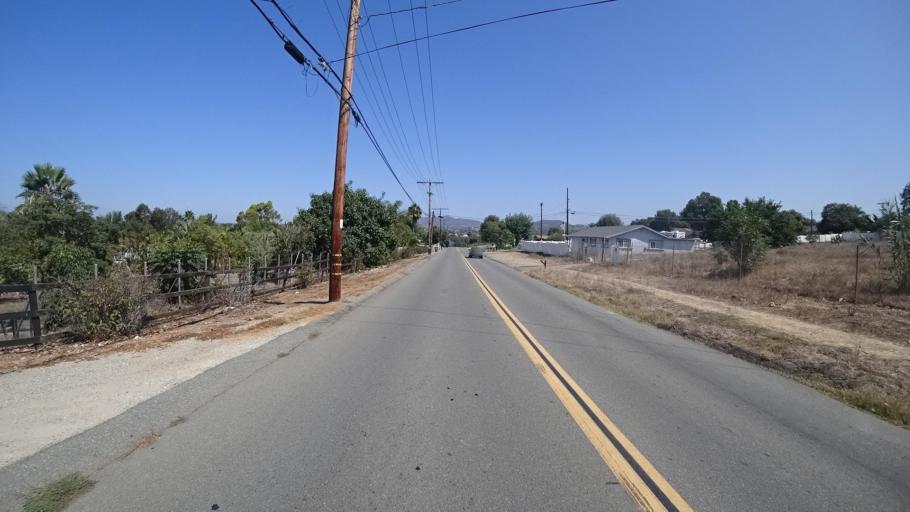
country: US
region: California
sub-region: San Diego County
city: Lake San Marcos
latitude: 33.1514
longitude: -117.2128
